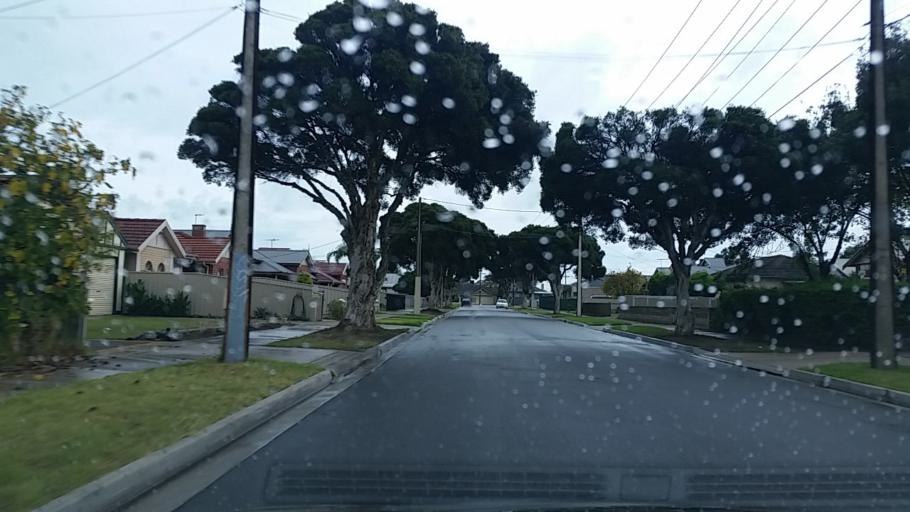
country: AU
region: South Australia
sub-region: Charles Sturt
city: Seaton
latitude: -34.8949
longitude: 138.5189
